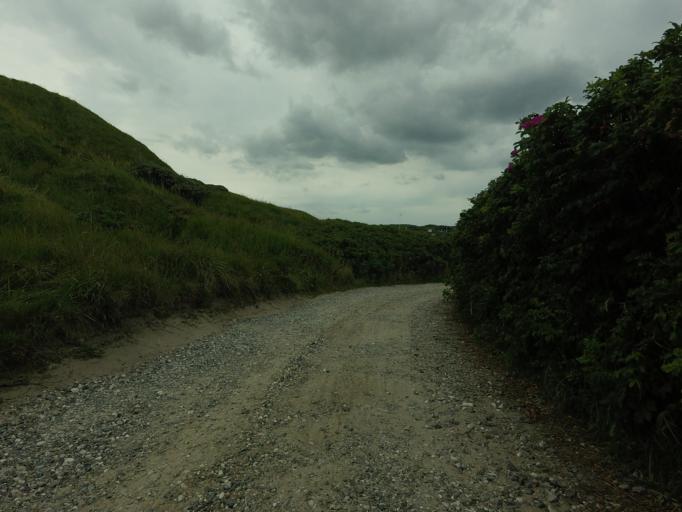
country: DK
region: North Denmark
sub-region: Jammerbugt Kommune
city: Pandrup
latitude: 57.3110
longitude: 9.6508
